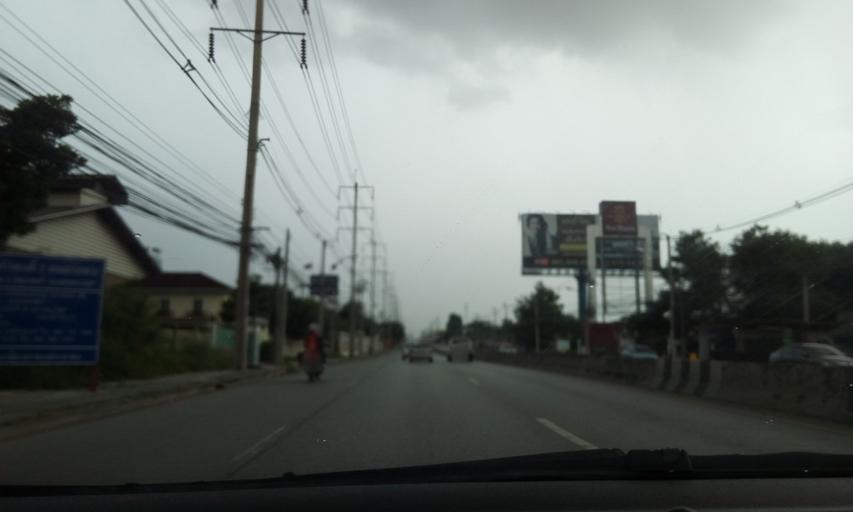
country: TH
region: Phra Nakhon Si Ayutthaya
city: Ban Bang Kadi Pathum Thani
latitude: 13.9554
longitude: 100.5499
